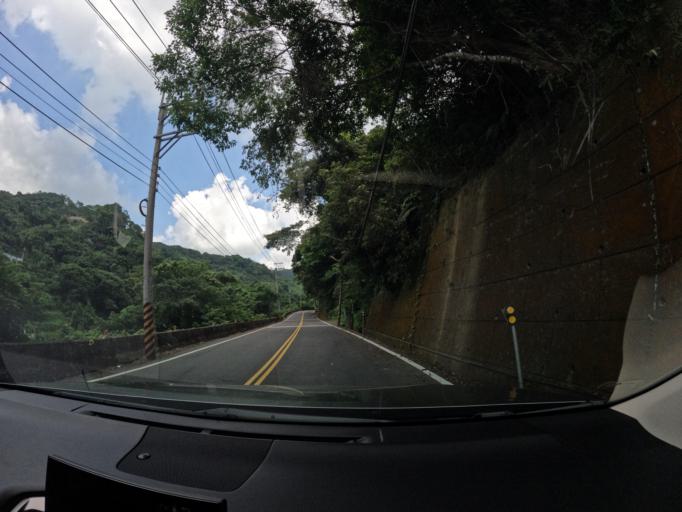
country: TW
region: Taiwan
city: Fengyuan
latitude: 24.3829
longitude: 120.8065
